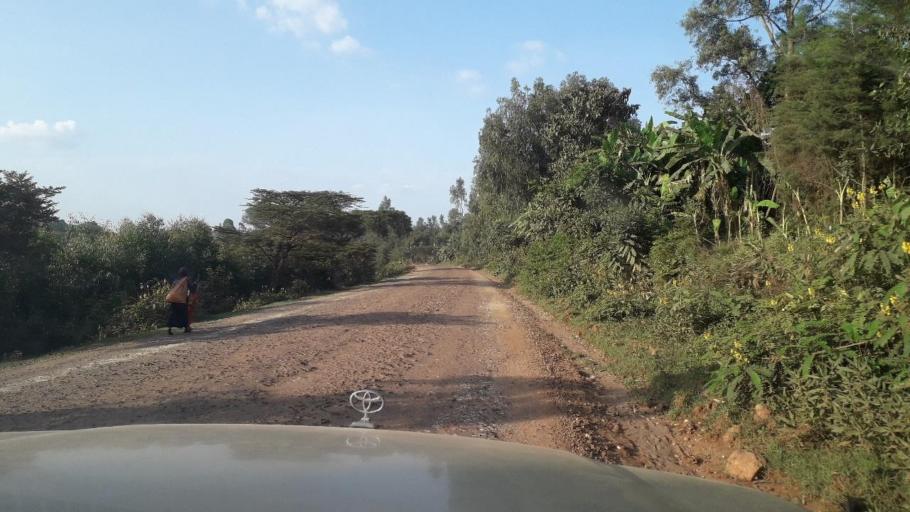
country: ET
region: Oromiya
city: Jima
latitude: 7.5784
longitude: 36.8584
